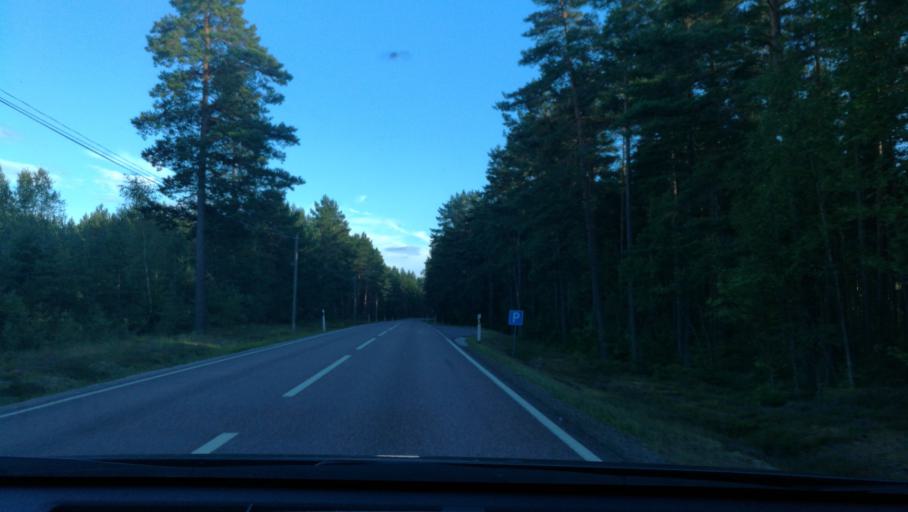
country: SE
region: Vaestmanland
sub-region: Kungsors Kommun
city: Kungsoer
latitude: 59.3078
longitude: 16.1075
